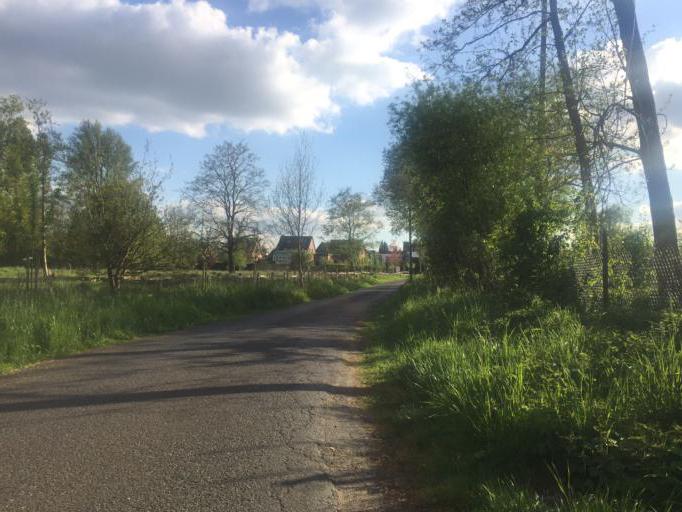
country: DE
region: North Rhine-Westphalia
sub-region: Regierungsbezirk Munster
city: Rheine
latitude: 52.2722
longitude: 7.4509
